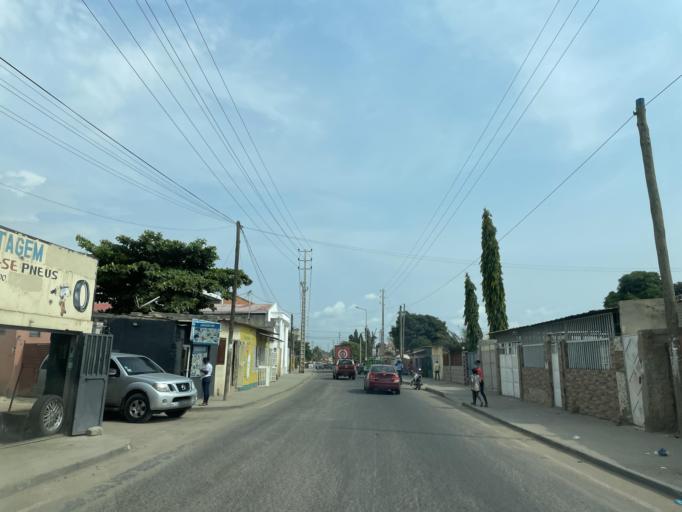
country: AO
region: Luanda
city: Luanda
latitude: -8.8983
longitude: 13.1912
